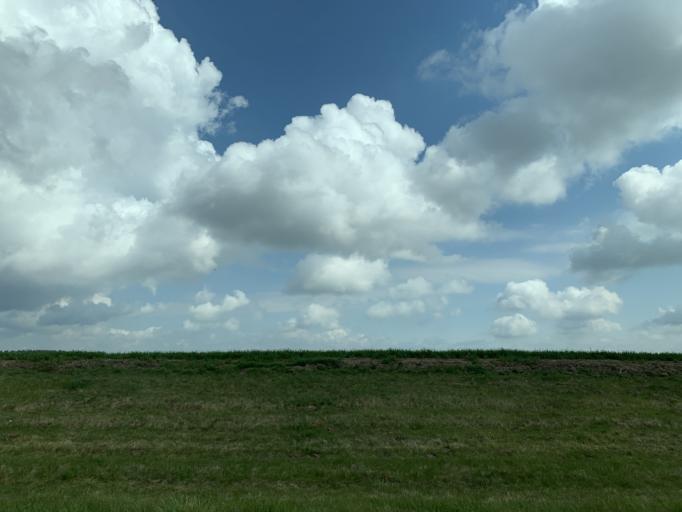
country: BY
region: Minsk
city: Nyasvizh
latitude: 53.2375
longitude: 26.7150
